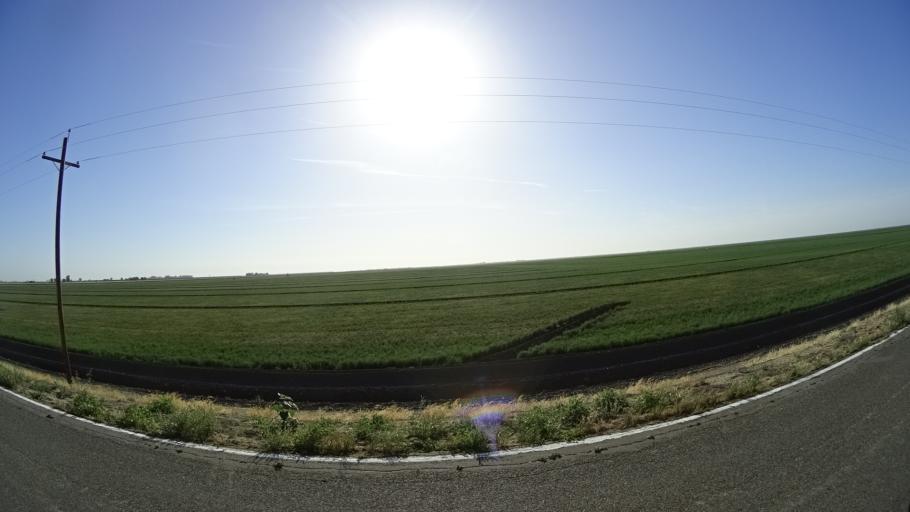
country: US
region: California
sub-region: Kings County
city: Stratford
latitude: 36.1497
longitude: -119.7981
